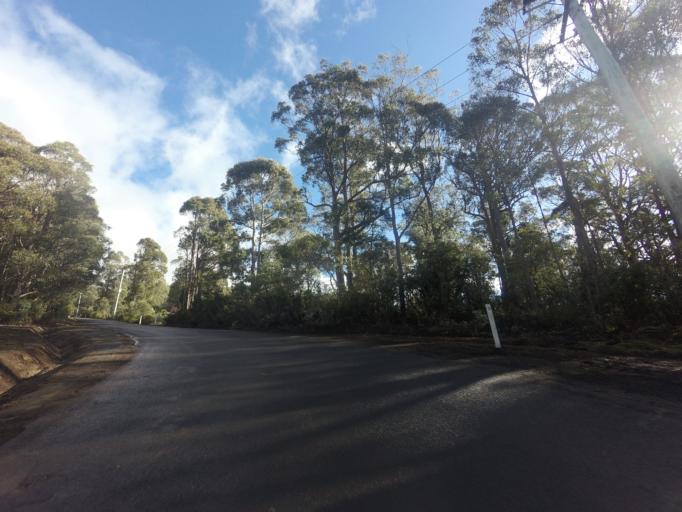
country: AU
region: Tasmania
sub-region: Glenorchy
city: Berriedale
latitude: -42.8373
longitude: 147.1601
